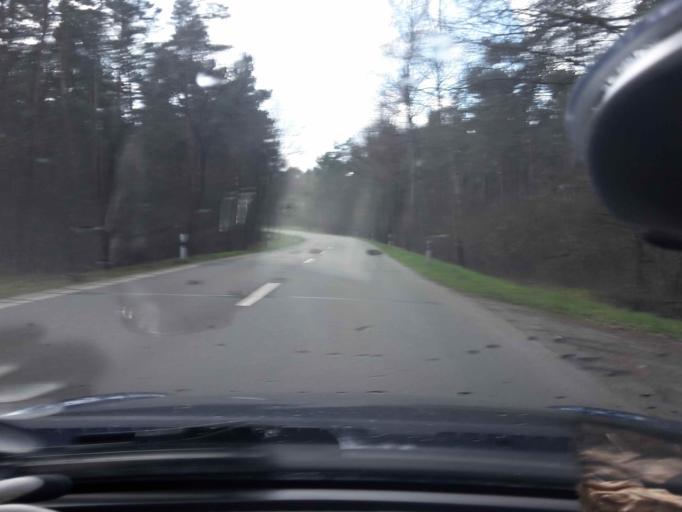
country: DE
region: Lower Saxony
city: Bispingen
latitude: 53.0782
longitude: 9.9671
